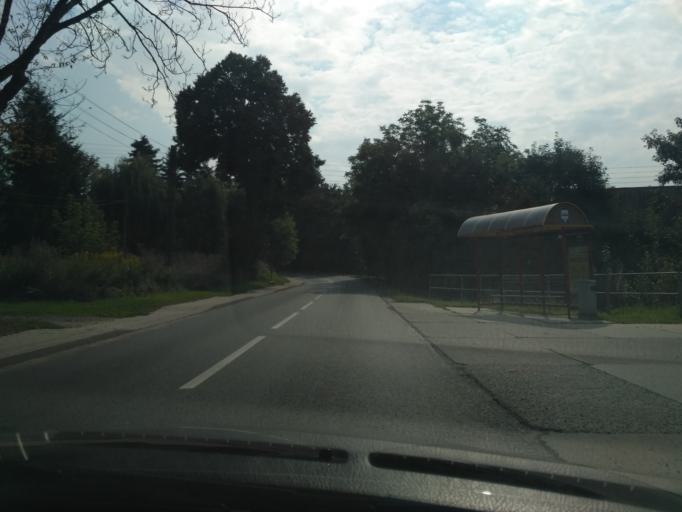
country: PL
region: Subcarpathian Voivodeship
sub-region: Powiat rzeszowski
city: Boguchwala
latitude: 50.0031
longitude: 21.9365
